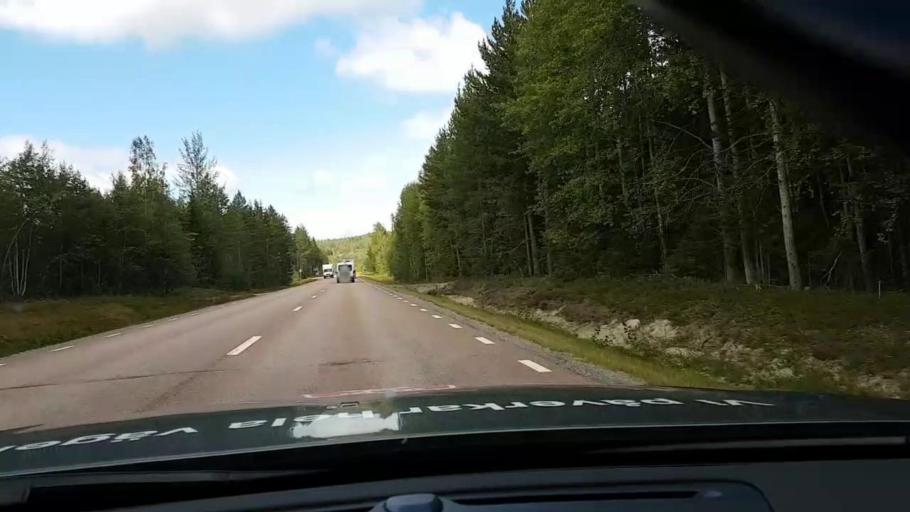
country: SE
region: Vaesternorrland
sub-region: OErnskoeldsviks Kommun
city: Bjasta
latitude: 63.3758
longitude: 18.4279
